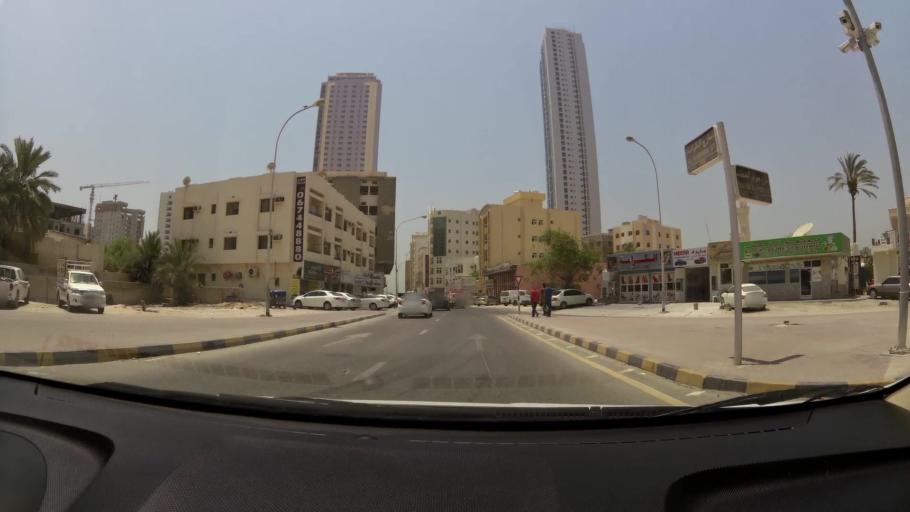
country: AE
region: Ajman
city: Ajman
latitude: 25.4089
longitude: 55.4366
